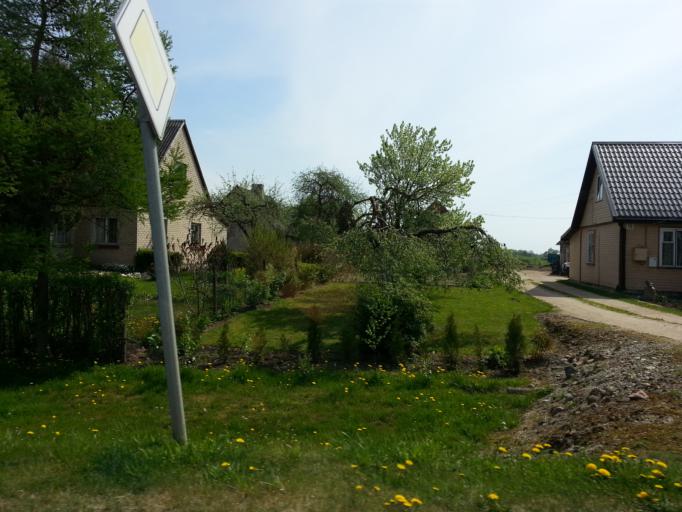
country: LT
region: Panevezys
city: Pasvalys
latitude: 55.9285
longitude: 24.2395
